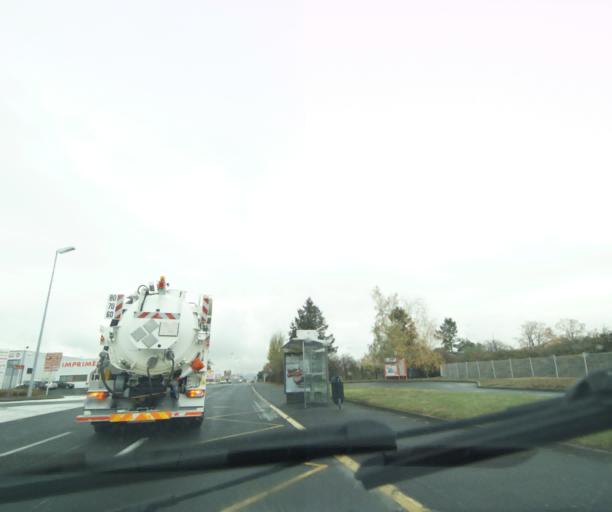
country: FR
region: Auvergne
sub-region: Departement du Puy-de-Dome
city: Perignat-les-Sarlieve
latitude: 45.7465
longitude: 3.1634
